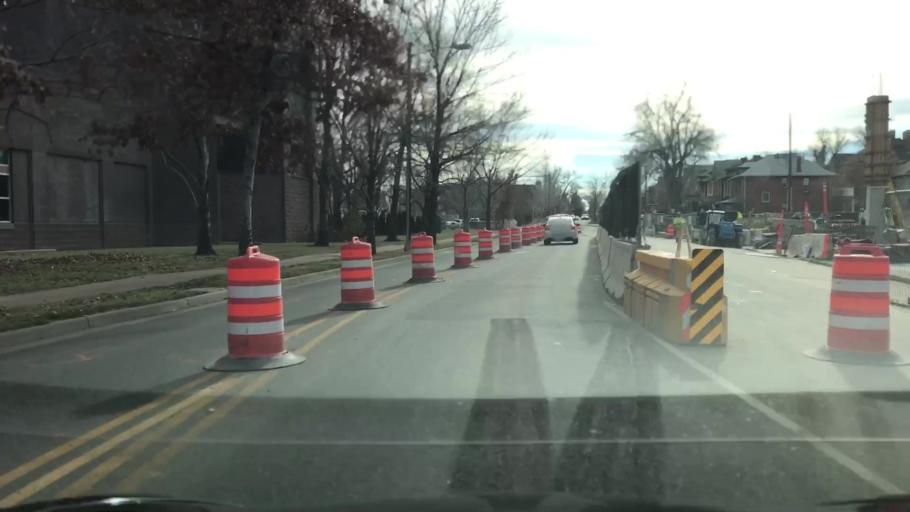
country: US
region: Colorado
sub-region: Denver County
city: Denver
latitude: 39.7219
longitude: -104.9827
